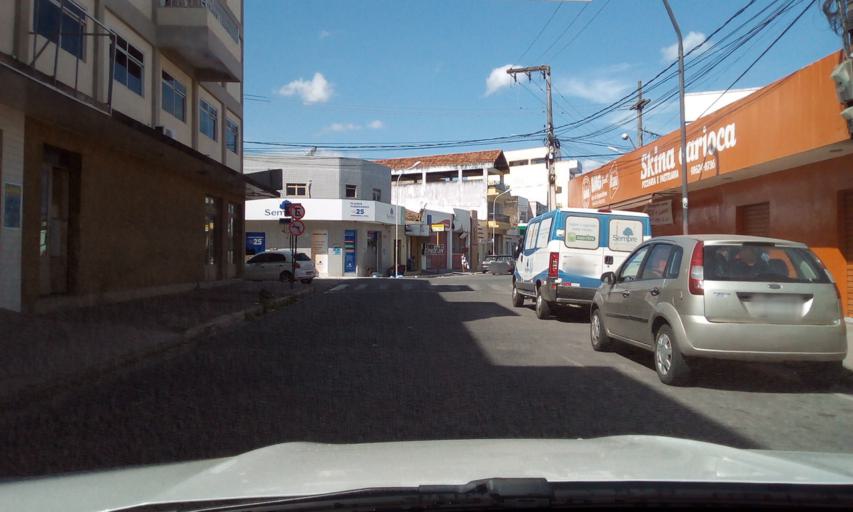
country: BR
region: Paraiba
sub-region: Guarabira
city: Guarabira
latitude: -6.8527
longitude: -35.4933
